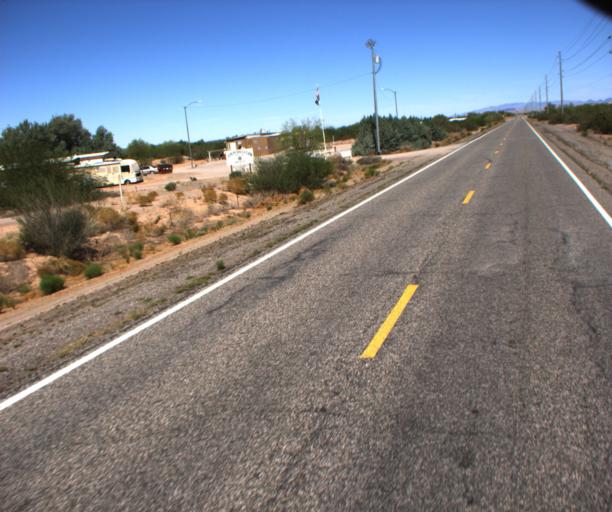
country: US
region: Arizona
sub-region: La Paz County
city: Cienega Springs
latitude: 33.9471
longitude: -114.0173
